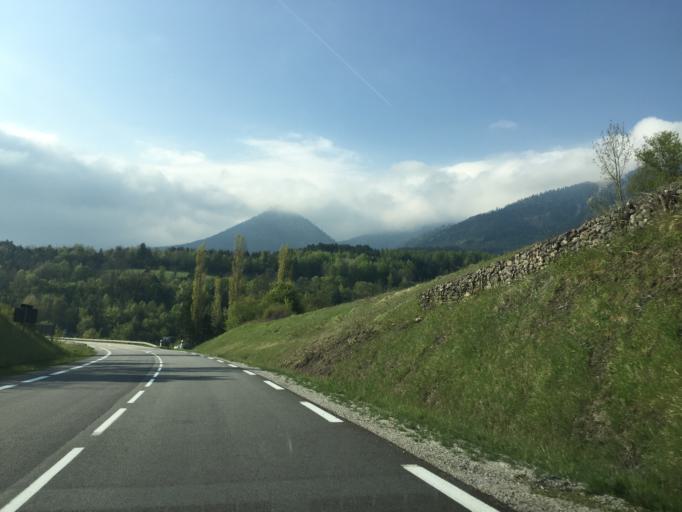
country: FR
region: Rhone-Alpes
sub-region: Departement de l'Isere
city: Mens
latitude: 44.7902
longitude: 5.6338
